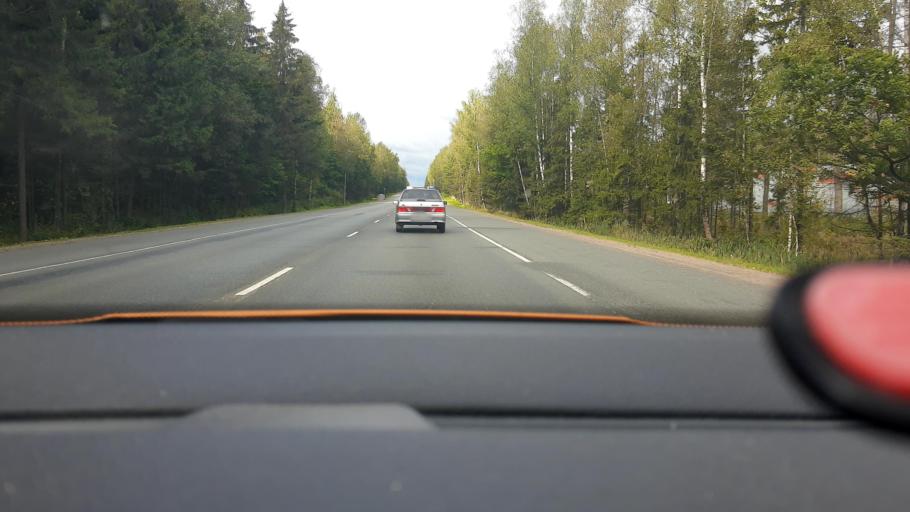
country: RU
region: Moskovskaya
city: Zelenogradskiy
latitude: 56.0908
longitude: 37.9881
